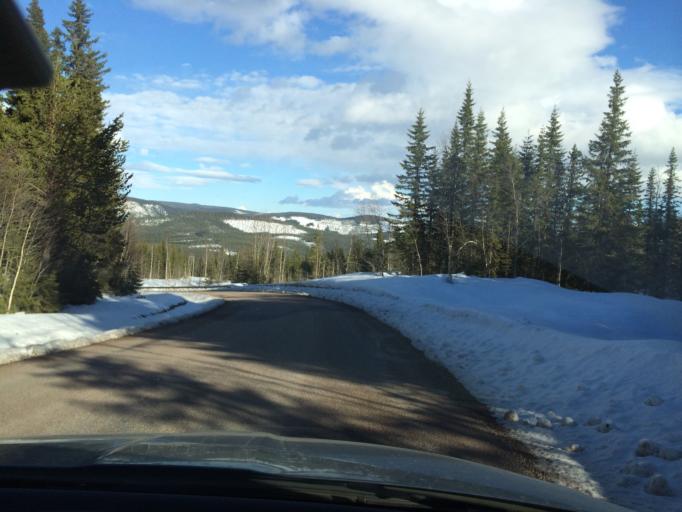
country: NO
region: Hedmark
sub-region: Trysil
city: Innbygda
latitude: 61.3405
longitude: 12.1950
